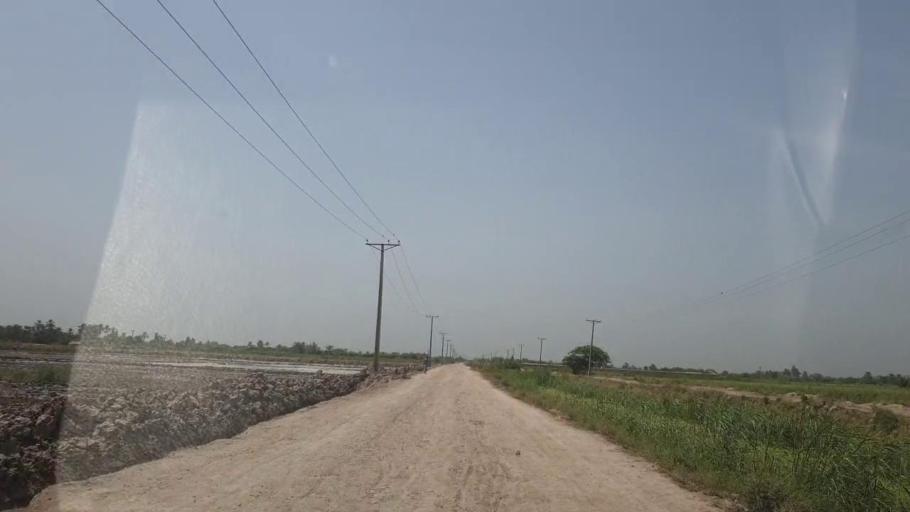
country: PK
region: Sindh
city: Ranipur
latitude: 27.3037
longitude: 68.5452
